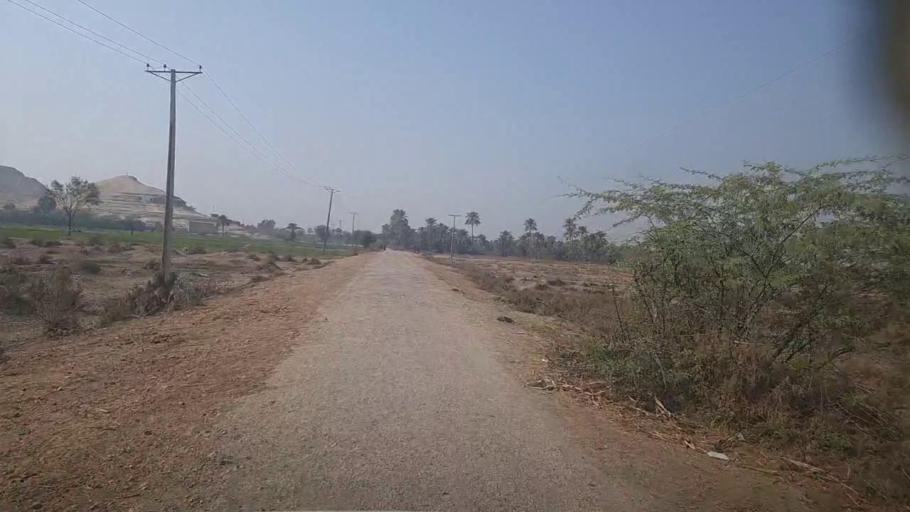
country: PK
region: Sindh
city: Kot Diji
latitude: 27.3484
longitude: 68.7221
